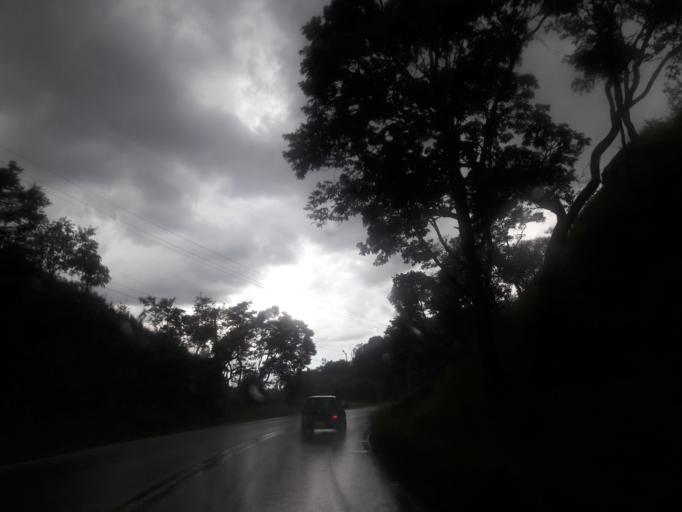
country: BR
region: Sao Paulo
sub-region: Bom Jesus Dos Perdoes
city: Bom Jesus dos Perdoes
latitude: -23.1946
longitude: -46.3928
